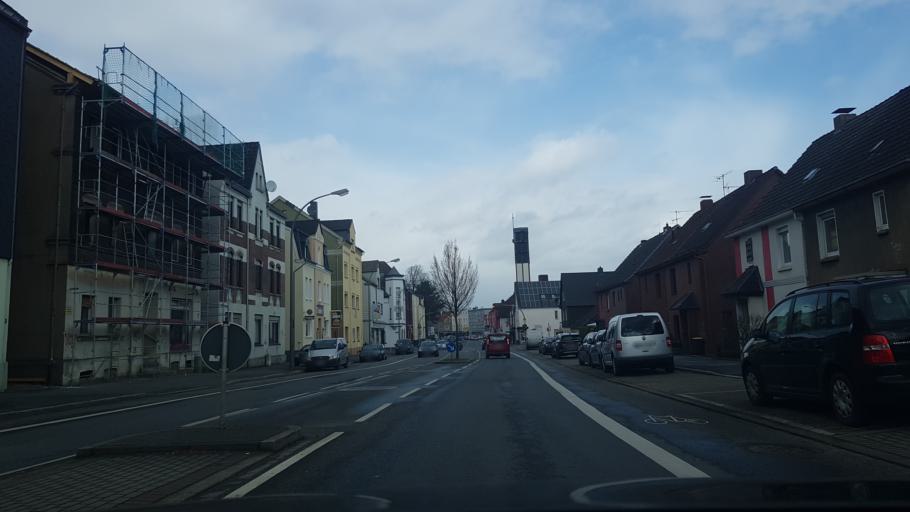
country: DE
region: North Rhine-Westphalia
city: Castrop-Rauxel
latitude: 51.5170
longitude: 7.3237
